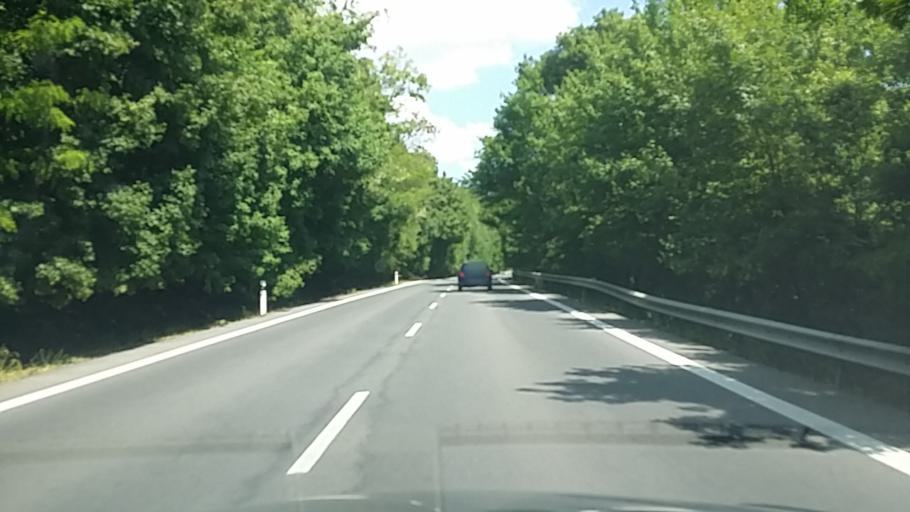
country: SK
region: Banskobystricky
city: Dudince
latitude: 48.2429
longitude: 18.9641
